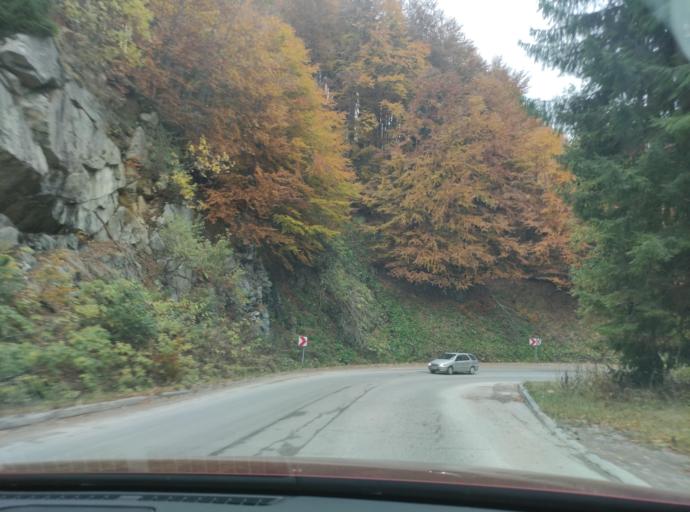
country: BG
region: Montana
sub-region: Obshtina Berkovitsa
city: Berkovitsa
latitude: 43.1276
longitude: 23.1345
